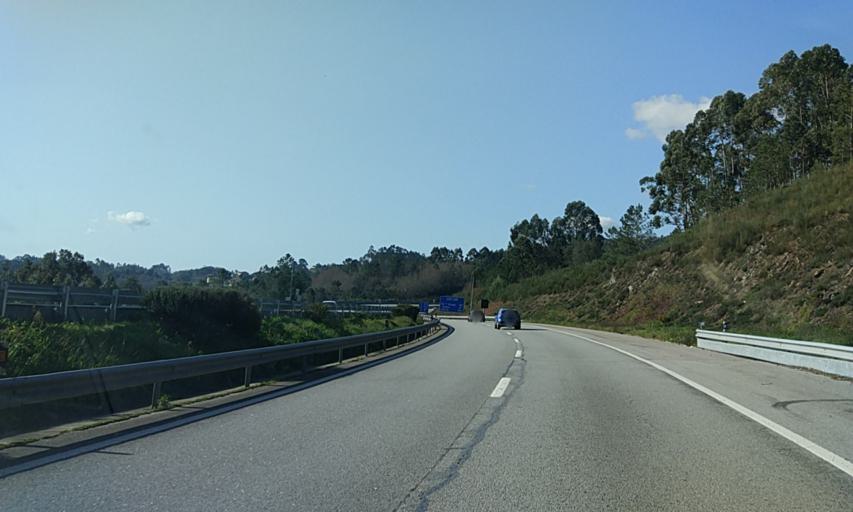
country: PT
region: Viseu
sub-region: Oliveira de Frades
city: Oliveira de Frades
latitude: 40.6812
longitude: -8.2700
